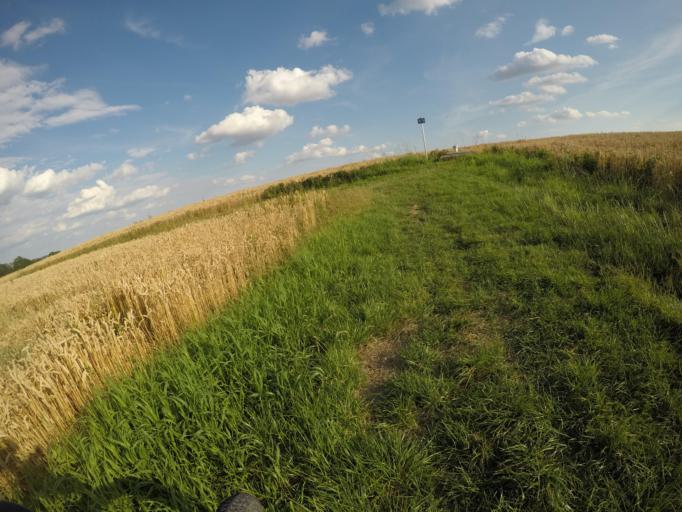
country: DE
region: Bavaria
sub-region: Lower Bavaria
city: Tiefenbach
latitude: 48.5080
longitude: 12.1237
